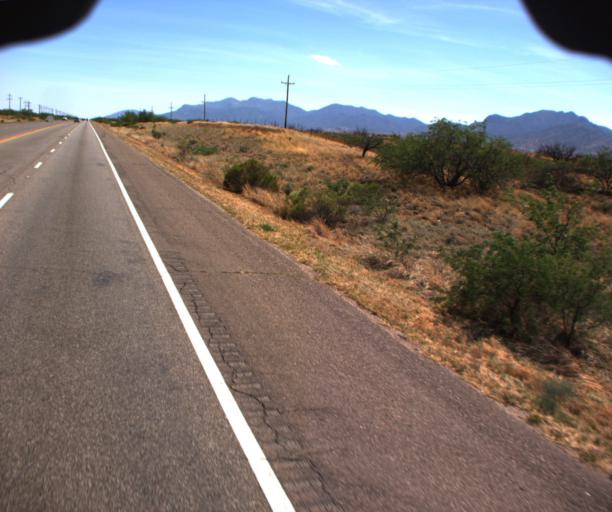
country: US
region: Arizona
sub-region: Cochise County
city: Huachuca City
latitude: 31.6099
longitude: -110.3318
